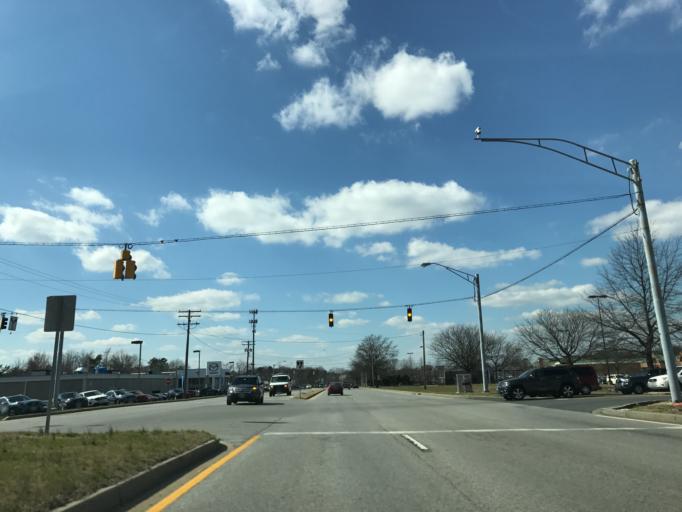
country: US
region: Maryland
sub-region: Anne Arundel County
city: South Gate
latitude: 39.1352
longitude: -76.5925
